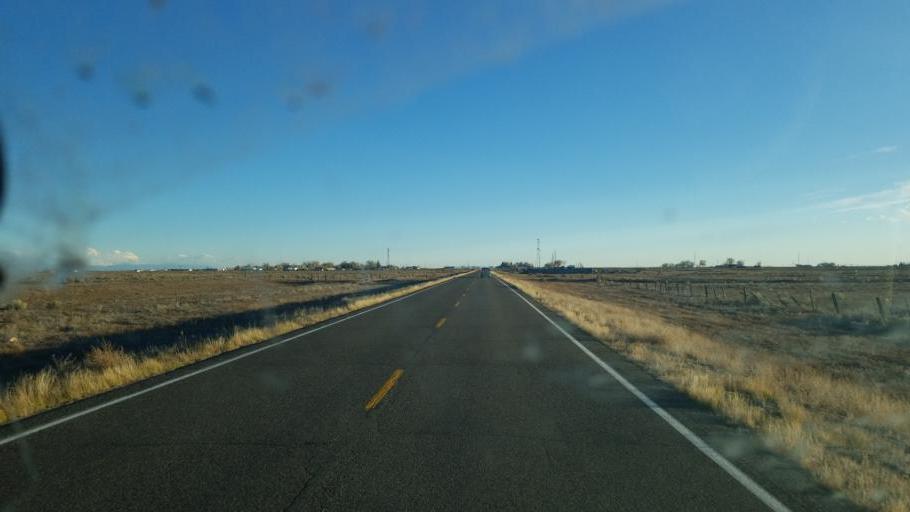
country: US
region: Colorado
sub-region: Saguache County
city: Center
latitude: 37.7581
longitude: -105.8819
